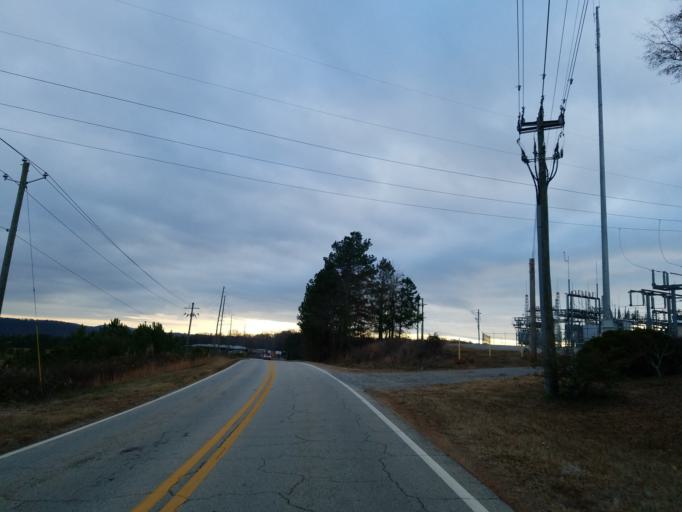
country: US
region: Georgia
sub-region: Dawson County
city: Dawsonville
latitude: 34.3708
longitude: -84.0388
